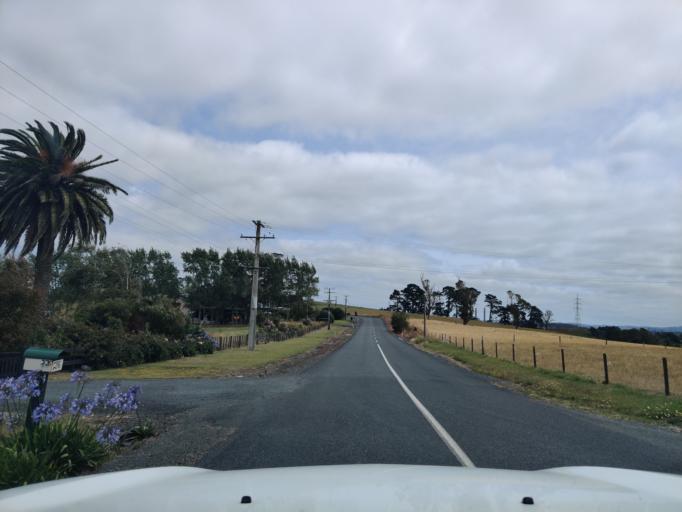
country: NZ
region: Waikato
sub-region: Waikato District
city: Te Kauwhata
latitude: -37.5124
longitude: 175.1766
